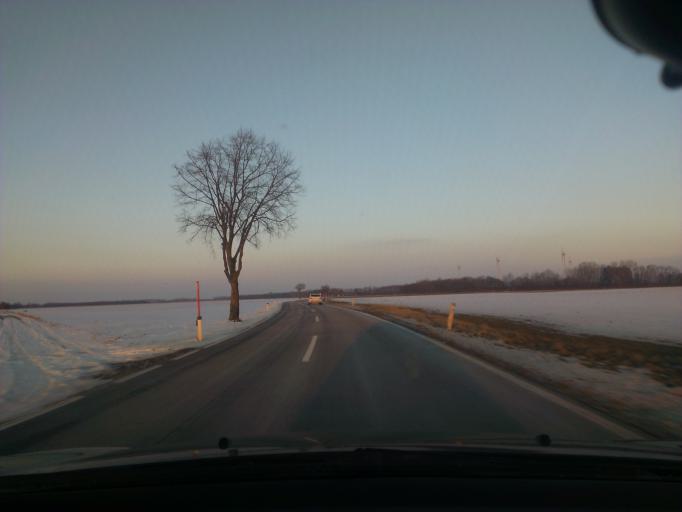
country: AT
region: Lower Austria
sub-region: Politischer Bezirk Baden
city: Mitterndorf an der Fischa
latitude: 47.9628
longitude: 16.4559
